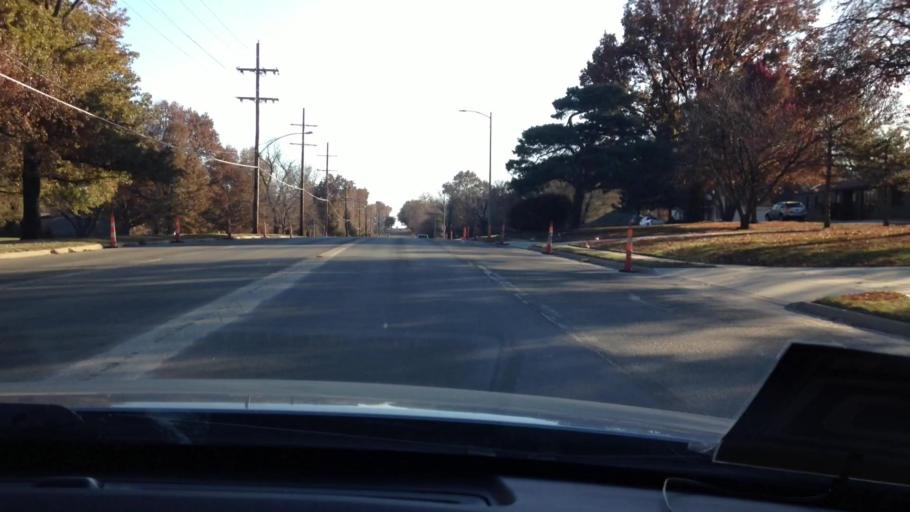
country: US
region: Kansas
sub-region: Johnson County
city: Leawood
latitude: 38.9697
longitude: -94.6304
